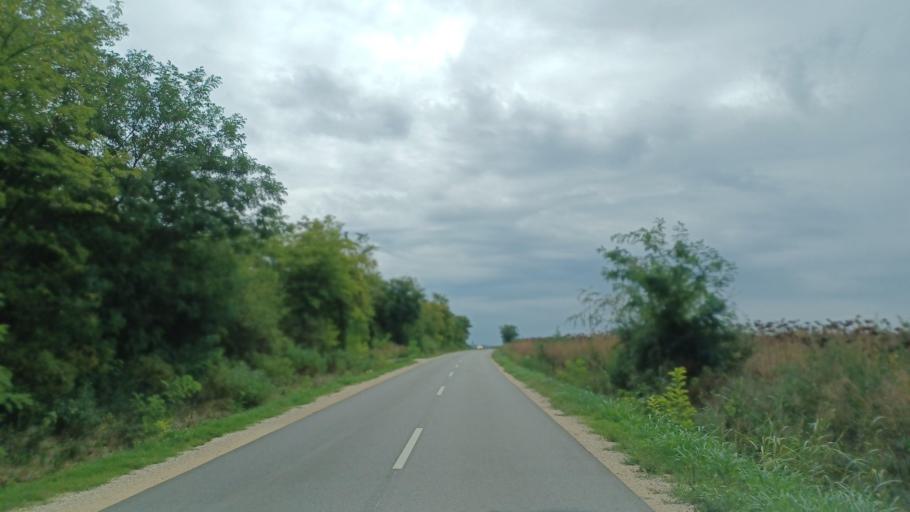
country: HU
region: Tolna
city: Szentgalpuszta
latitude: 46.4129
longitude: 18.6130
